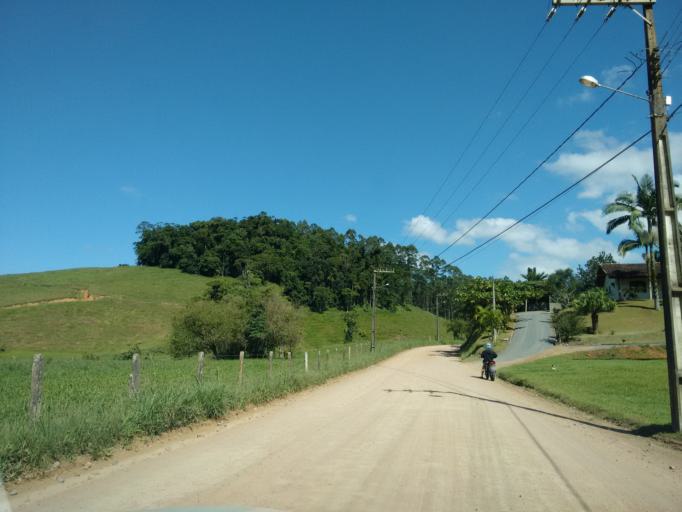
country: BR
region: Santa Catarina
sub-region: Pomerode
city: Pomerode
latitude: -26.8210
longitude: -49.1726
